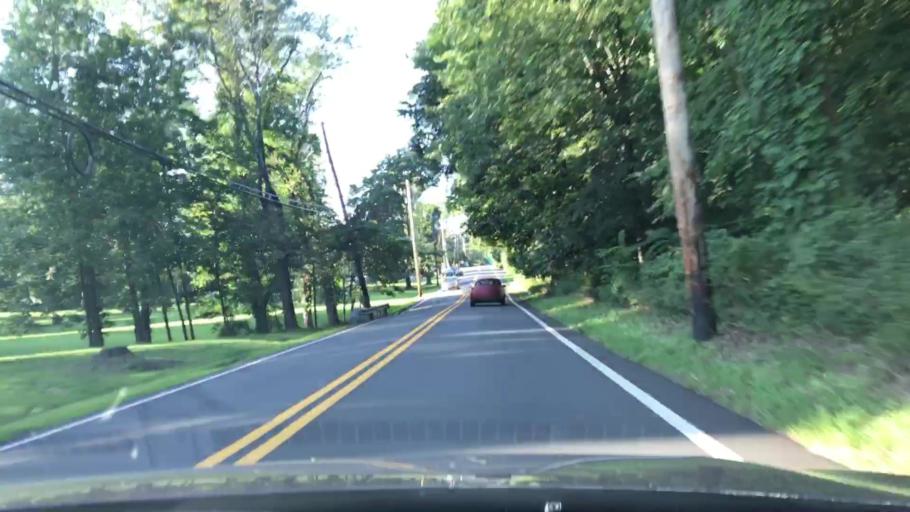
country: US
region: New Jersey
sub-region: Bergen County
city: Northvale
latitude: 41.0062
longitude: -73.9298
